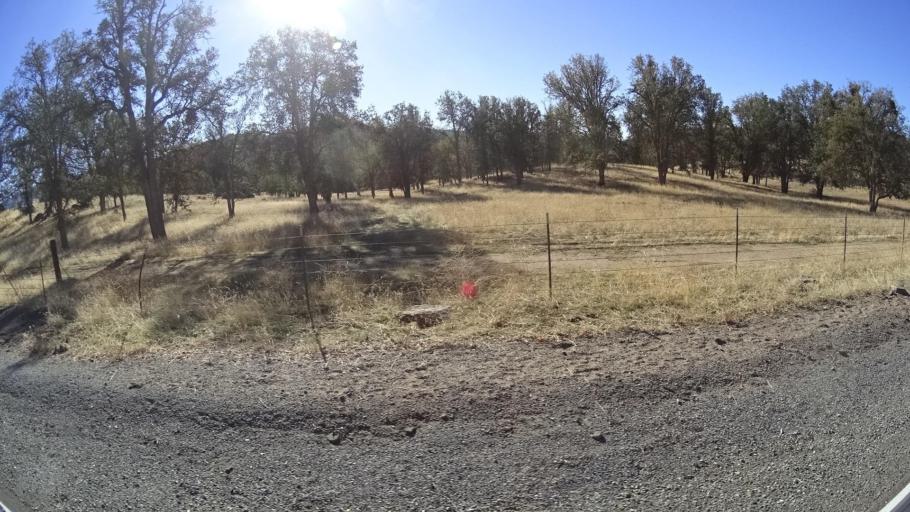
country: US
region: California
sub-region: Kern County
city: Alta Sierra
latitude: 35.7118
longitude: -118.7329
